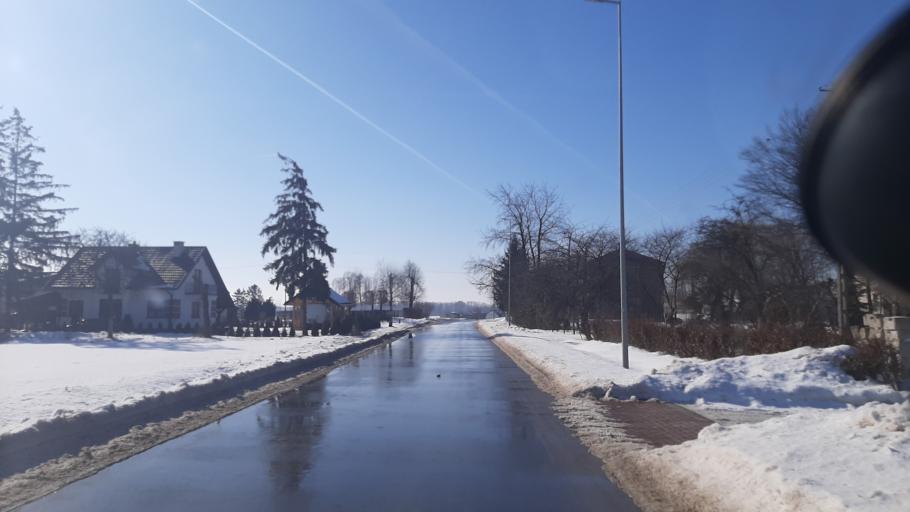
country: PL
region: Lublin Voivodeship
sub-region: Powiat lubelski
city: Garbow
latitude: 51.3285
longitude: 22.3294
